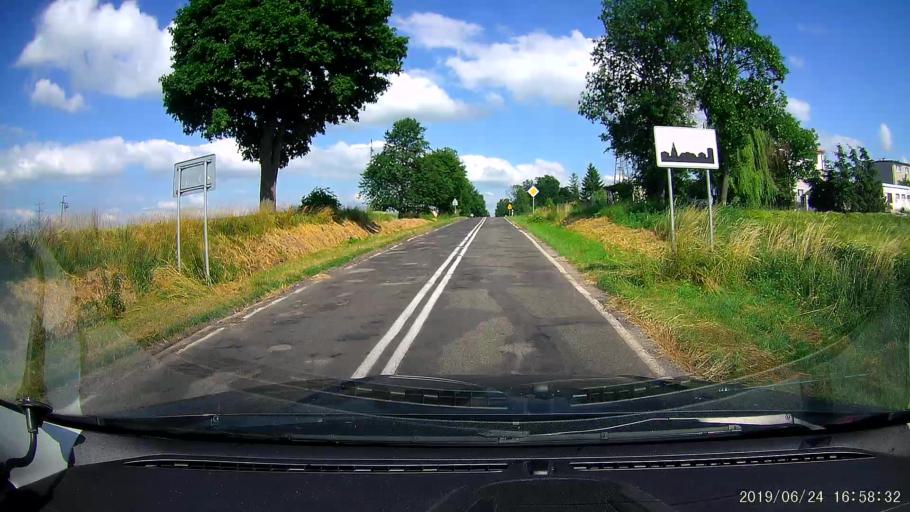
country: PL
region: Lublin Voivodeship
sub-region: Powiat tomaszowski
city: Telatyn
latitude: 50.5250
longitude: 23.8830
